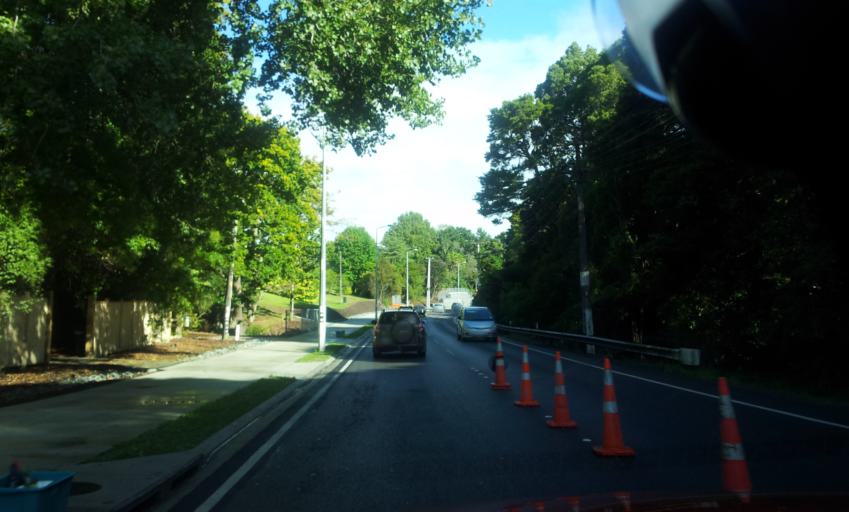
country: NZ
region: Auckland
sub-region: Auckland
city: Warkworth
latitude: -36.3954
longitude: 174.6583
